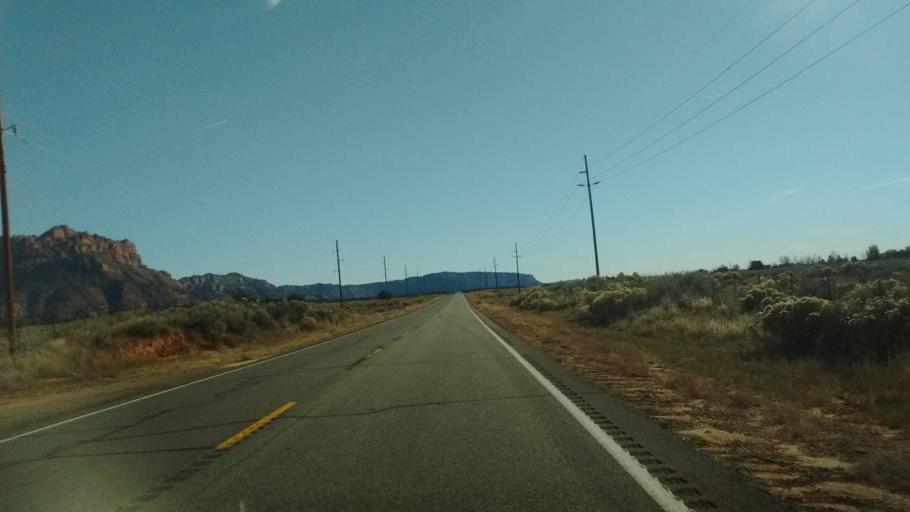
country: US
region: Arizona
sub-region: Mohave County
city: Colorado City
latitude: 37.0321
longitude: -113.0594
